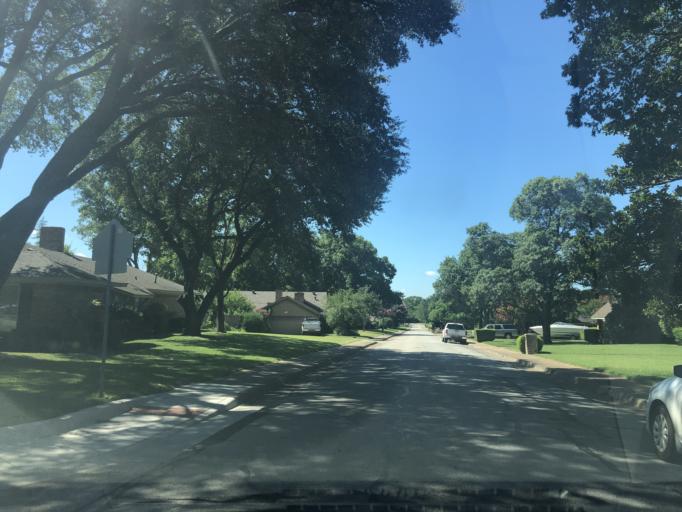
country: US
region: Texas
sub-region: Dallas County
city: Duncanville
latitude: 32.6397
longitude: -96.9301
